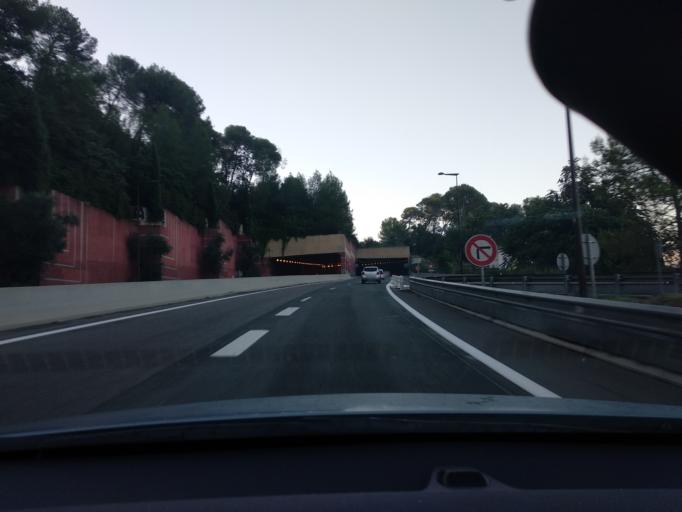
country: FR
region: Provence-Alpes-Cote d'Azur
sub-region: Departement des Alpes-Maritimes
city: Grasse
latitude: 43.6406
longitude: 6.9359
